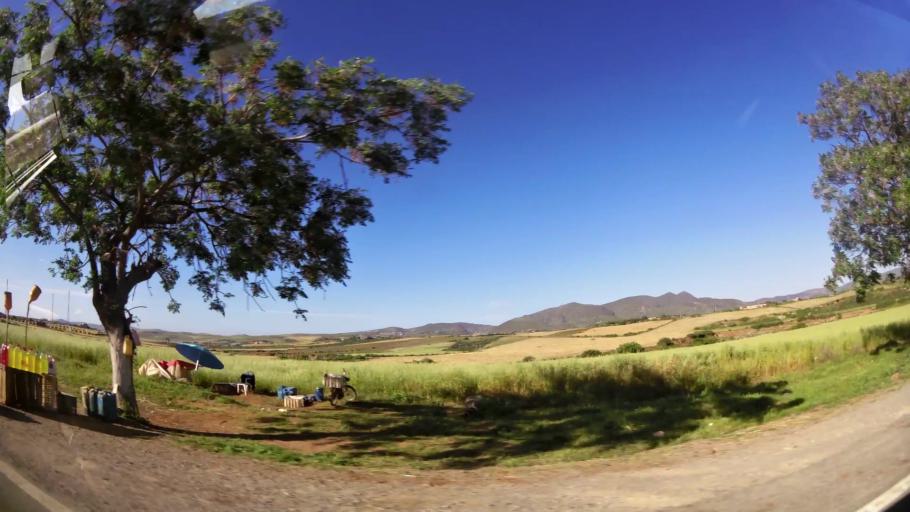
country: MA
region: Oriental
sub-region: Berkane-Taourirt
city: Ahfir
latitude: 34.9832
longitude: -2.1434
